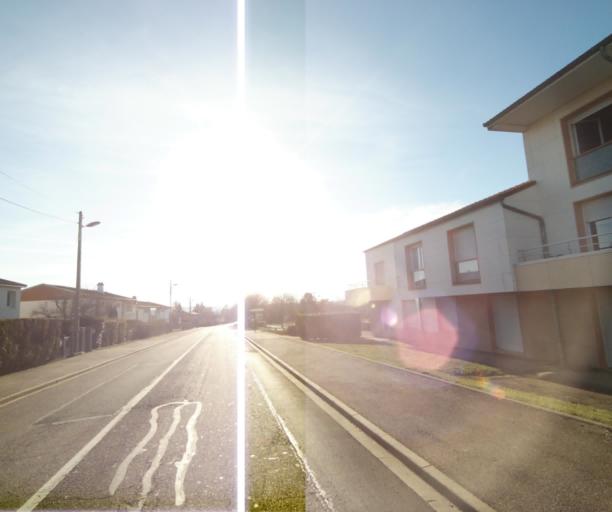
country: FR
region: Lorraine
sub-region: Departement de Meurthe-et-Moselle
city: Seichamps
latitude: 48.7138
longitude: 6.2607
